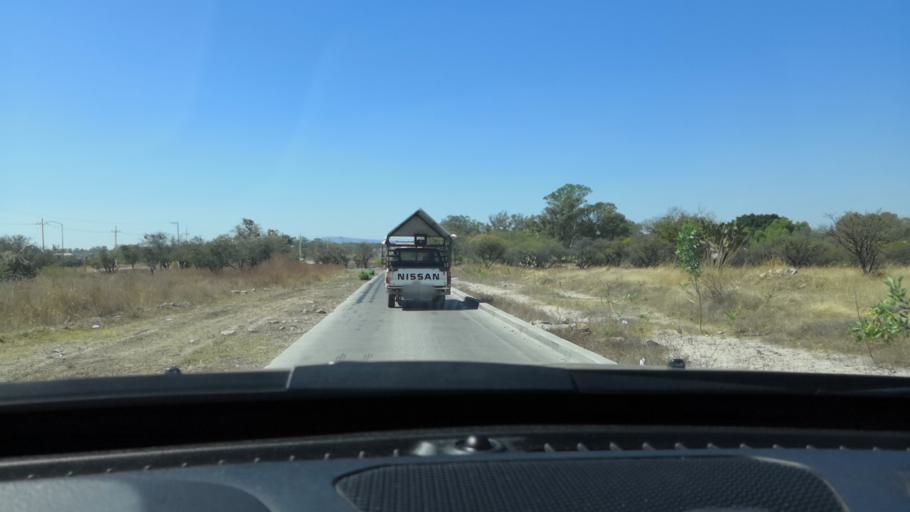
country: MX
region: Guanajuato
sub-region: Leon
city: Centro Familiar la Soledad
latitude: 21.1025
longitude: -101.7730
